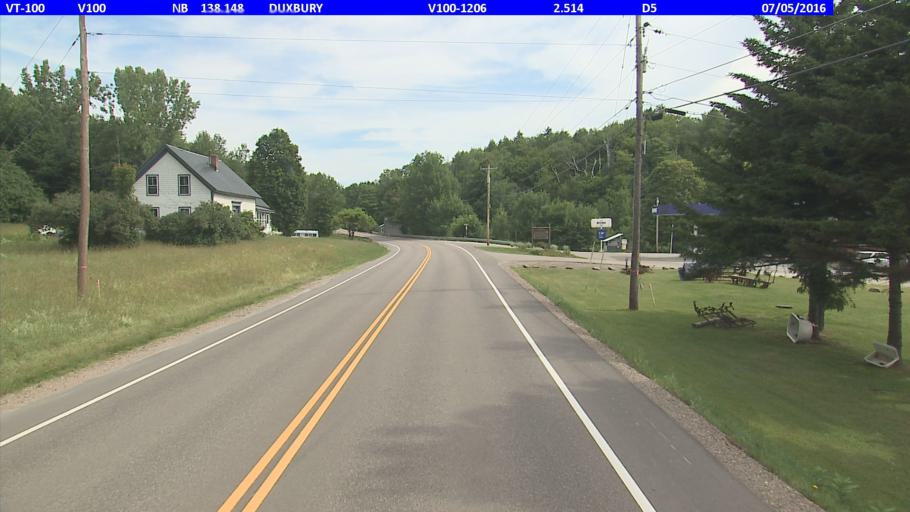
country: US
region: Vermont
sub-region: Washington County
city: Waterbury
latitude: 44.2817
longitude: -72.7826
